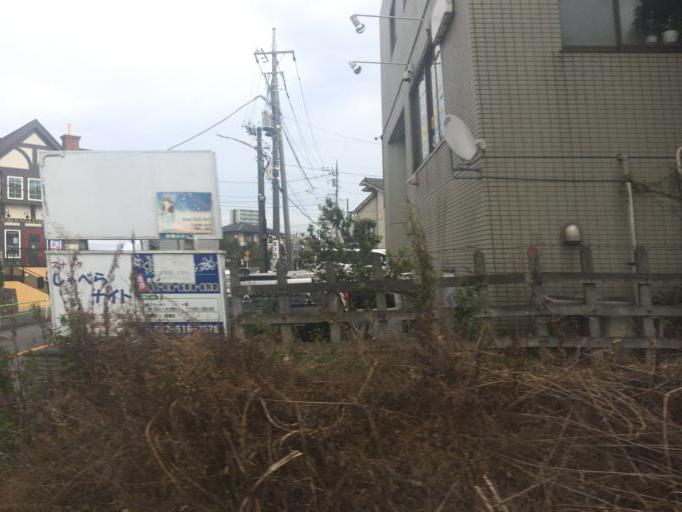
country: JP
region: Tokyo
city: Fussa
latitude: 35.7104
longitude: 139.3559
